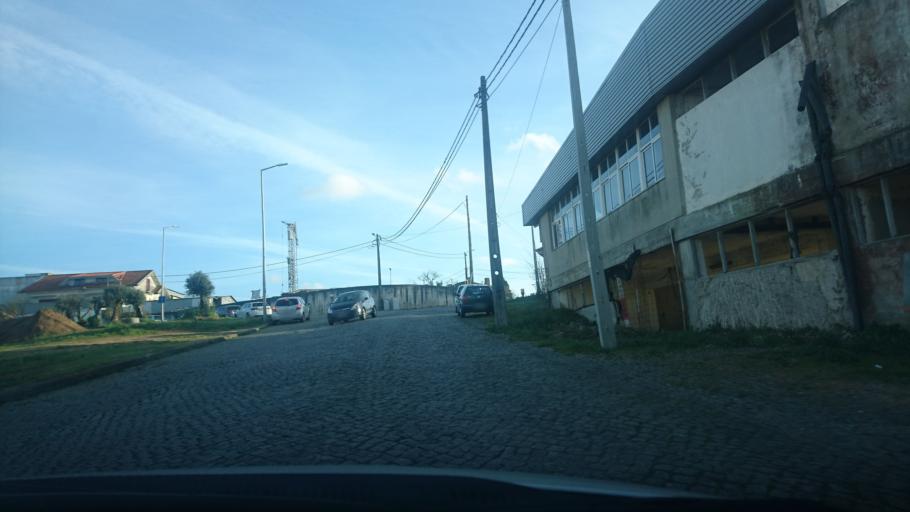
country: PT
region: Aveiro
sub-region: Santa Maria da Feira
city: Pacos de Brandao
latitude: 40.9863
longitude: -8.5963
